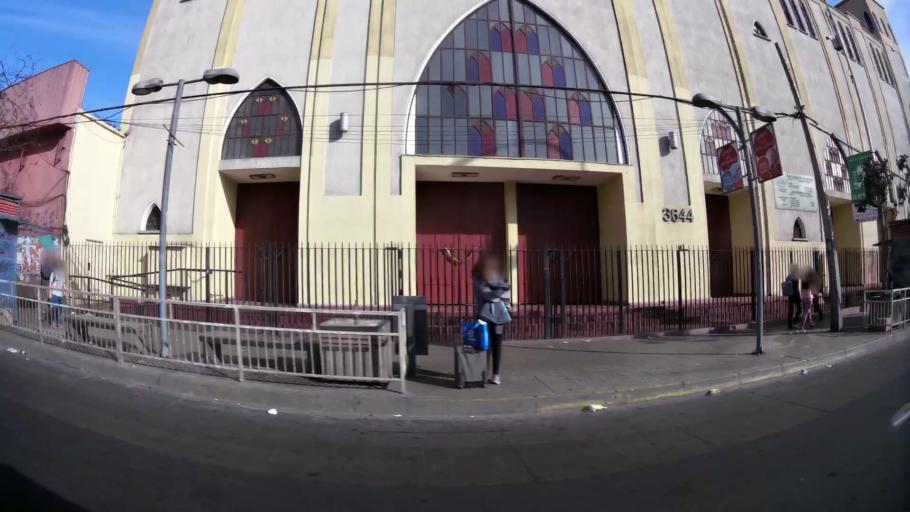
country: CL
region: Santiago Metropolitan
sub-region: Provincia de Santiago
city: Santiago
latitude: -33.4528
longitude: -70.6853
